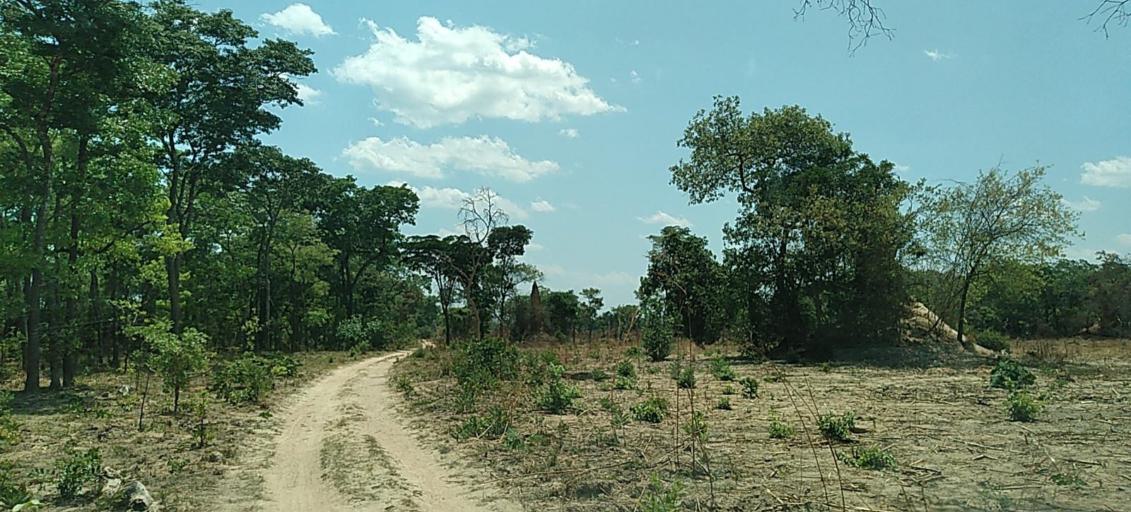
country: ZM
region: Central
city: Kapiri Mposhi
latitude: -13.6321
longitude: 28.7626
